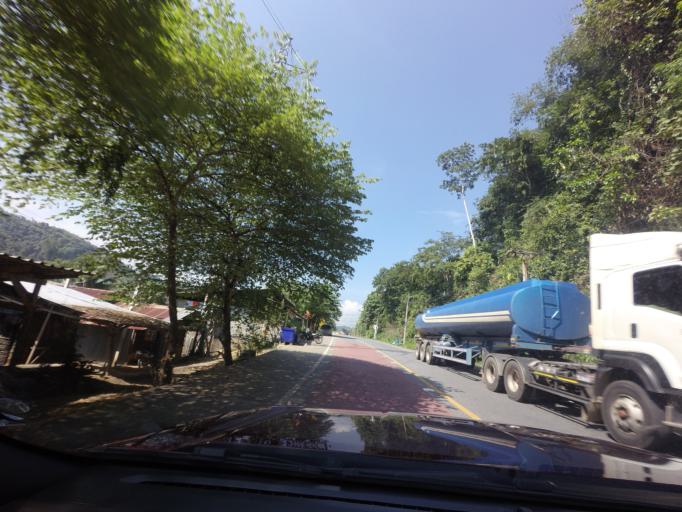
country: TH
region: Yala
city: Than To
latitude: 5.9640
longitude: 101.1951
